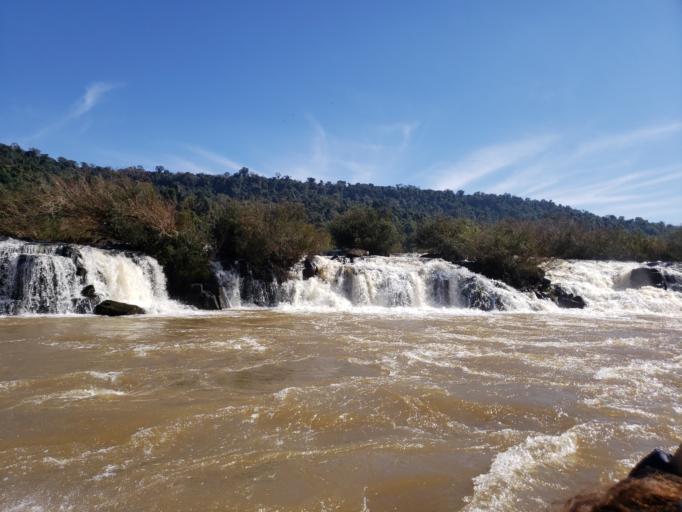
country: BR
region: Rio Grande do Sul
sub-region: Tres Passos
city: Tres Passos
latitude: -27.1513
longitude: -53.8877
